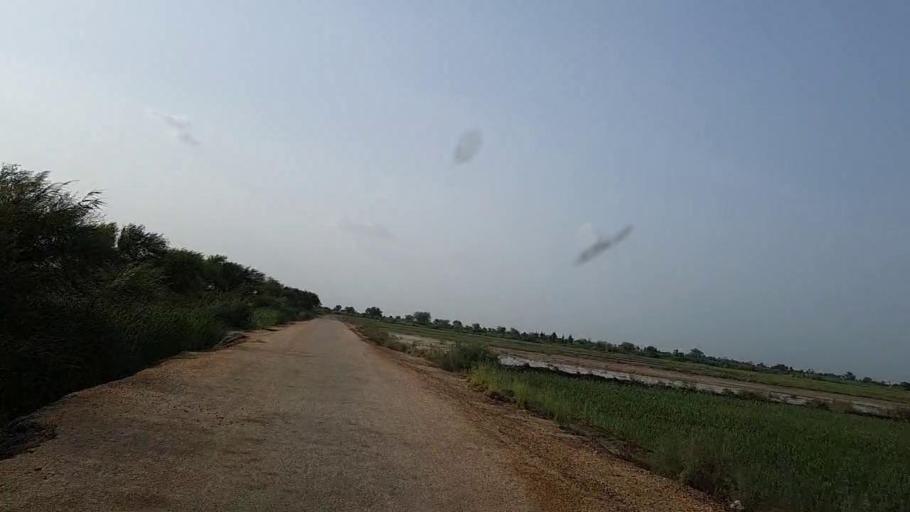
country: PK
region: Sindh
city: Kotri
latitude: 25.1867
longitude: 68.2497
